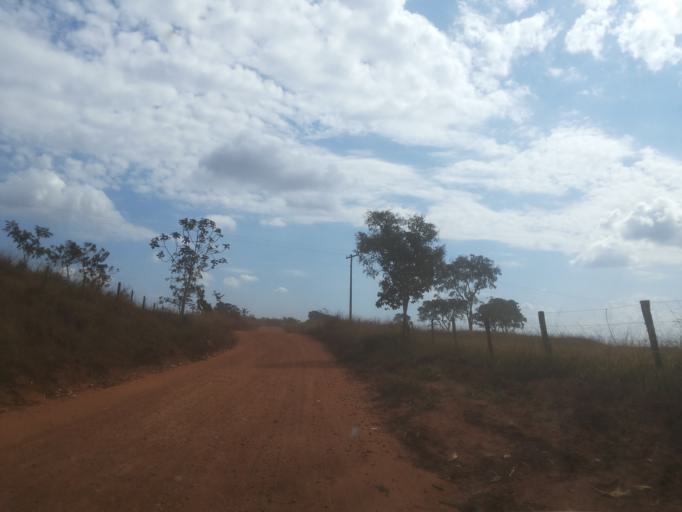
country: BR
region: Minas Gerais
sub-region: Ituiutaba
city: Ituiutaba
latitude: -18.9996
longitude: -49.4138
